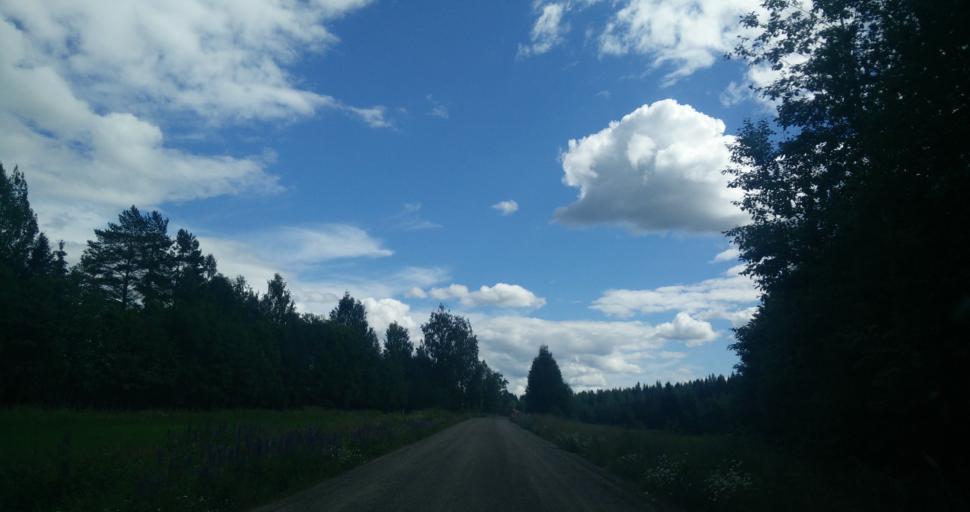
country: SE
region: Gaevleborg
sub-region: Nordanstigs Kommun
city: Bergsjoe
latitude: 62.0698
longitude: 16.7687
